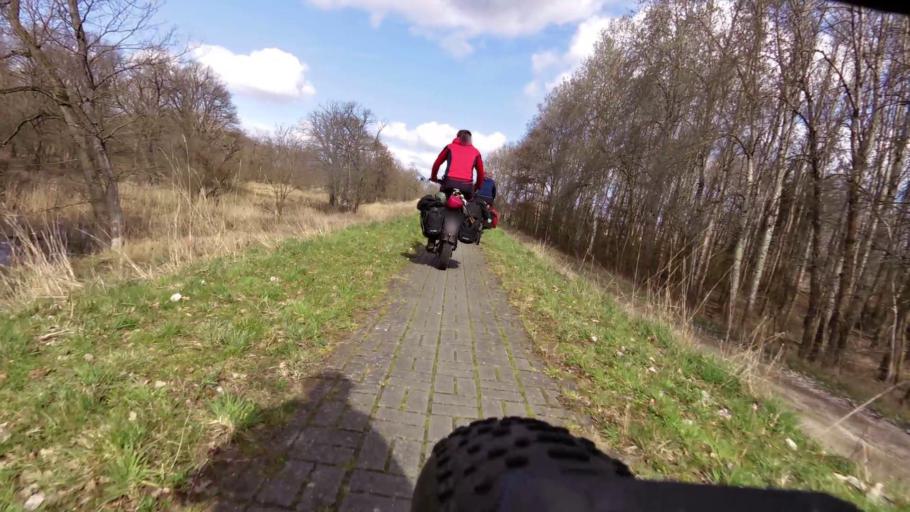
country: DE
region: Brandenburg
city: Lebus
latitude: 52.3985
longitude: 14.5420
